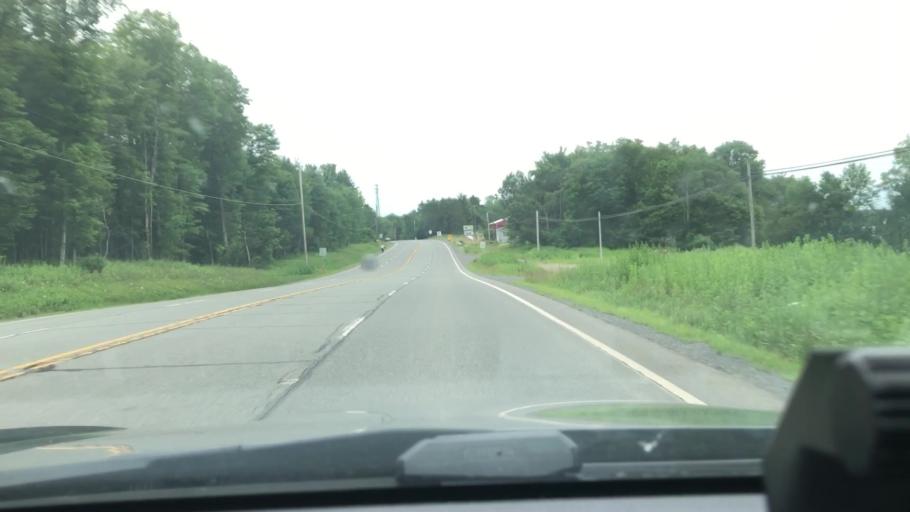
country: US
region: Pennsylvania
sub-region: Lackawanna County
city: Moscow
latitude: 41.2406
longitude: -75.5014
